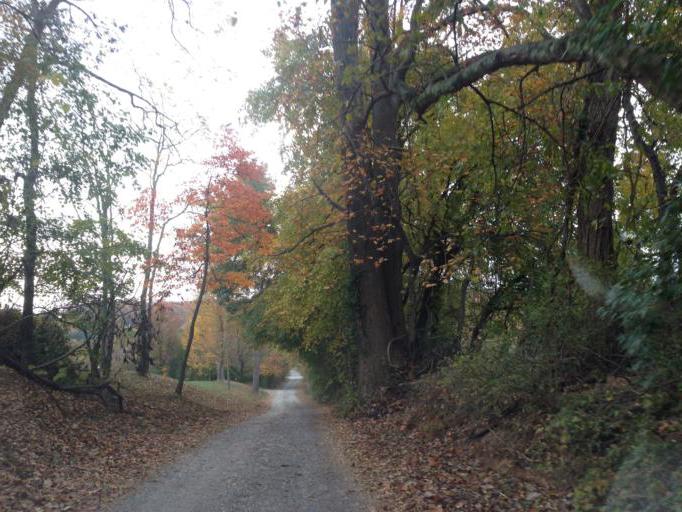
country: US
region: Maryland
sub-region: Howard County
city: Highland
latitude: 39.2585
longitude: -76.9645
